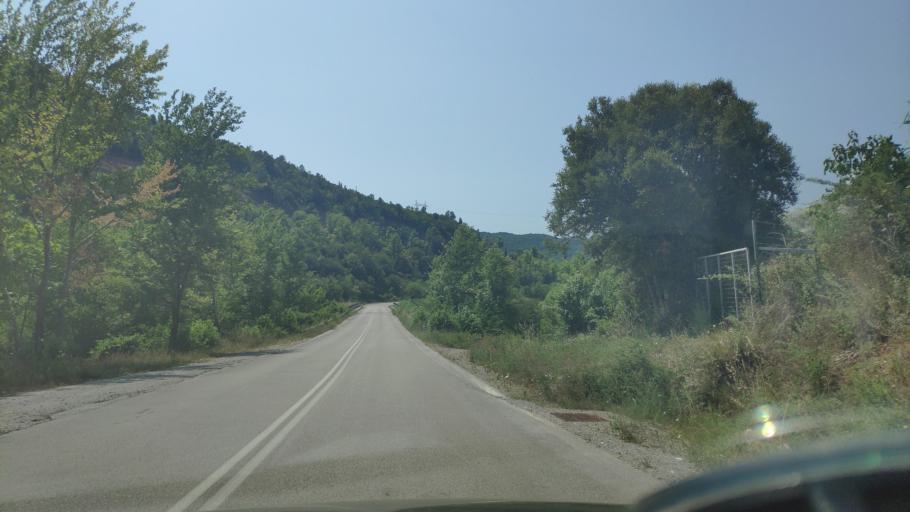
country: GR
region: Epirus
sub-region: Nomos Artas
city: Ano Kalentini
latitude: 39.2252
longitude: 21.1542
